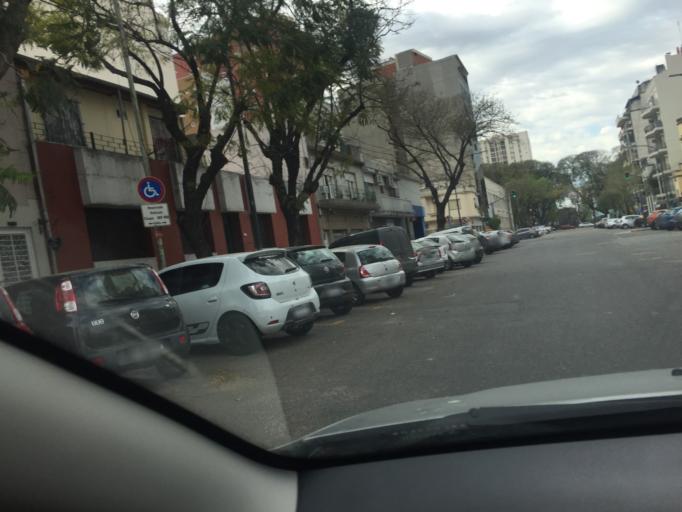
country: AR
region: Buenos Aires
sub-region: Partido de General San Martin
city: General San Martin
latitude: -34.5706
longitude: -58.4910
